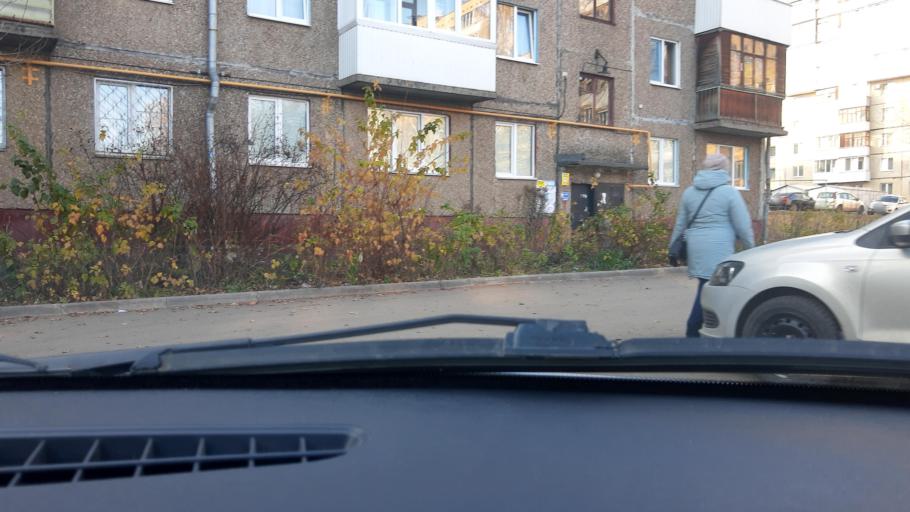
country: RU
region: Bashkortostan
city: Ufa
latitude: 54.8083
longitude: 56.1240
